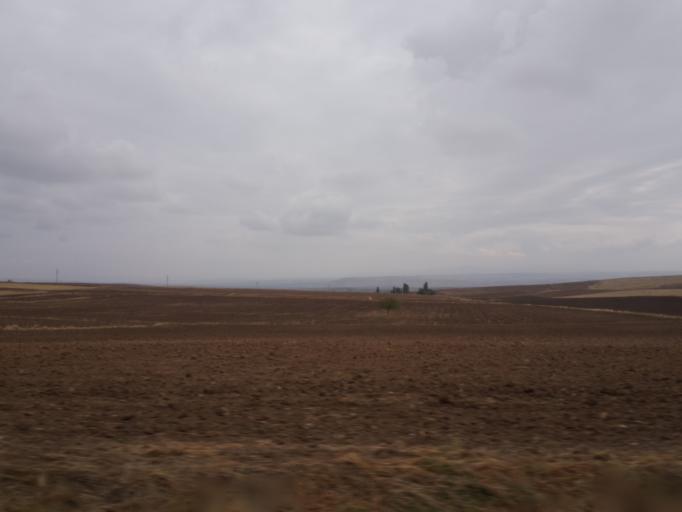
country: TR
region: Kirikkale
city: Celebi
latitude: 39.5156
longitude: 33.5479
